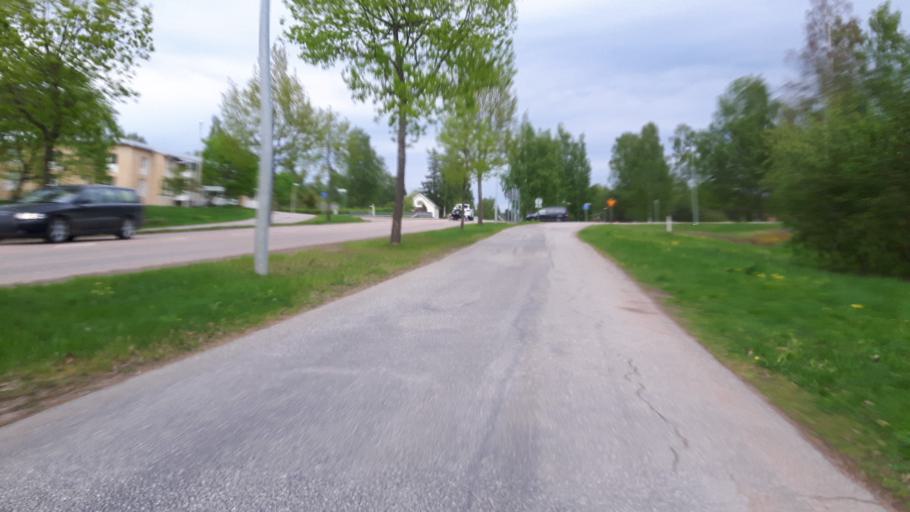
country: FI
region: Kymenlaakso
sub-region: Kotka-Hamina
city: Hamina
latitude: 60.5617
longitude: 27.2146
